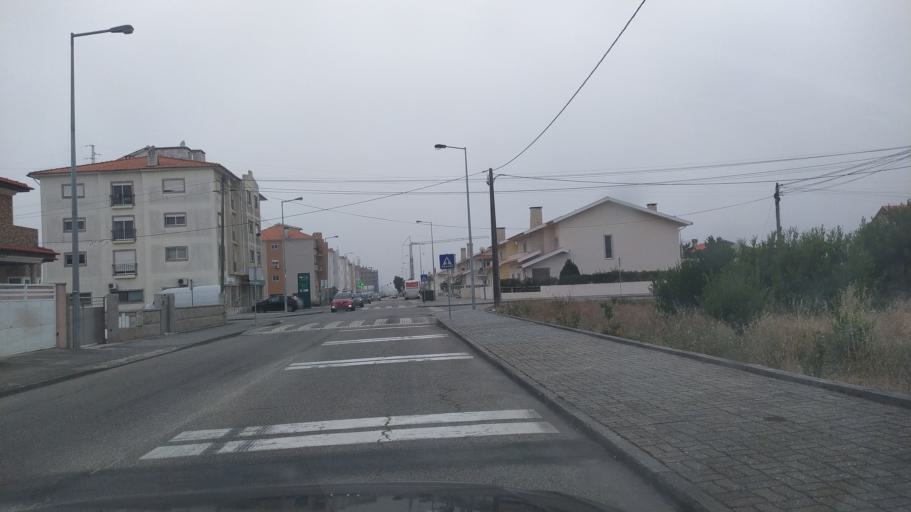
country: PT
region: Aveiro
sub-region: Ilhavo
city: Gafanha da Encarnacao
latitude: 40.5584
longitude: -8.7490
